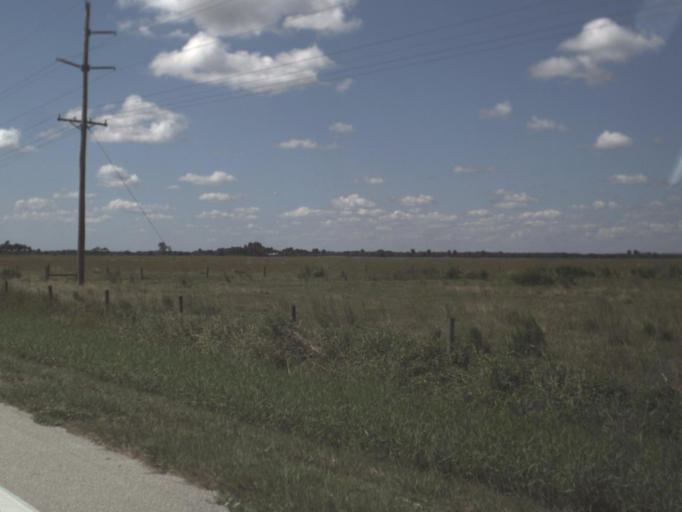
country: US
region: Florida
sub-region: Glades County
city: Moore Haven
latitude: 26.8123
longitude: -81.2303
